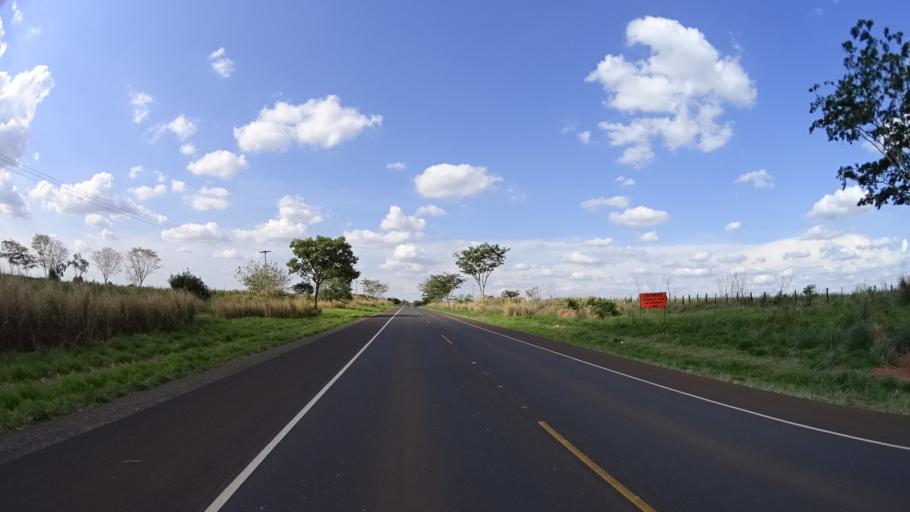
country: BR
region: Sao Paulo
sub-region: Urupes
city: Urupes
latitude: -21.0241
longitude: -49.2337
